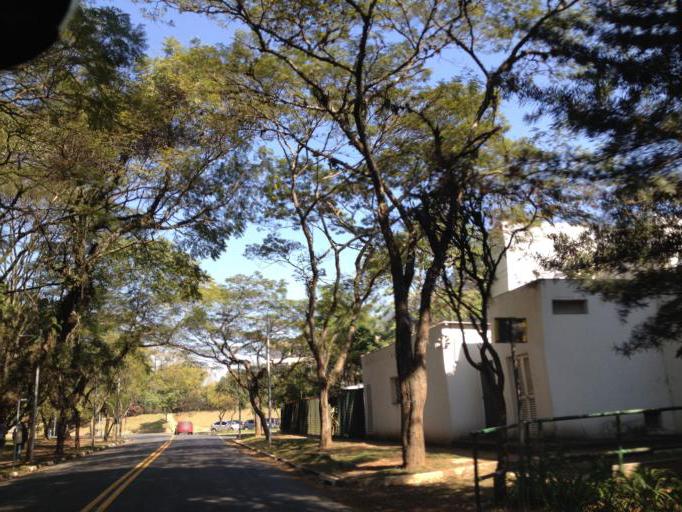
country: BR
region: Sao Paulo
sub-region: Osasco
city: Osasco
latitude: -23.5665
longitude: -46.7304
